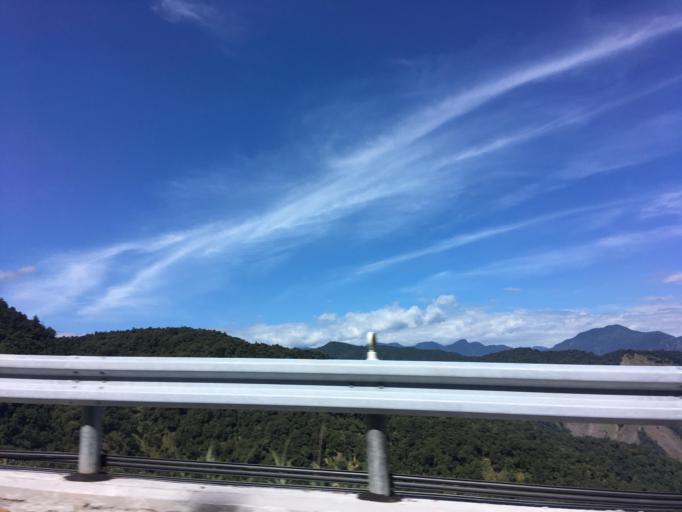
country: TW
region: Taiwan
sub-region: Yilan
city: Yilan
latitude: 24.5330
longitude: 121.5163
